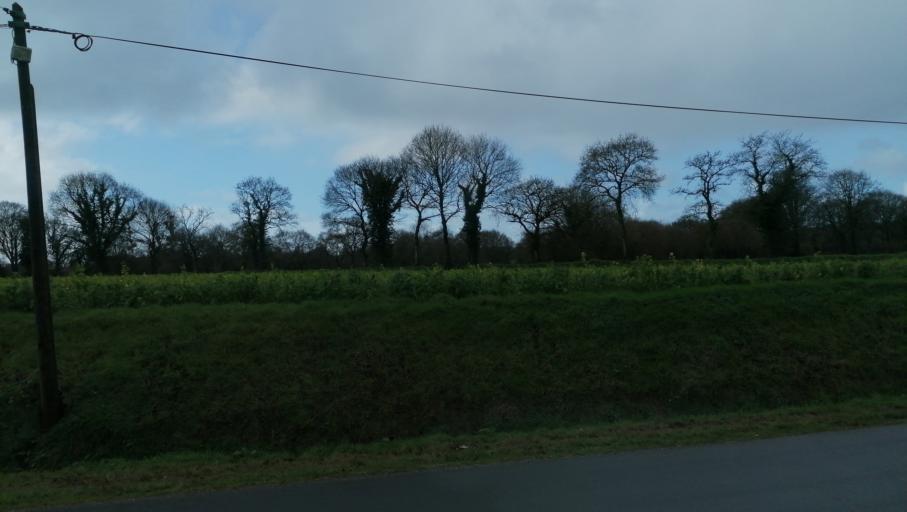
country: FR
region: Brittany
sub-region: Departement des Cotes-d'Armor
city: Lanrodec
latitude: 48.4922
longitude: -3.0044
